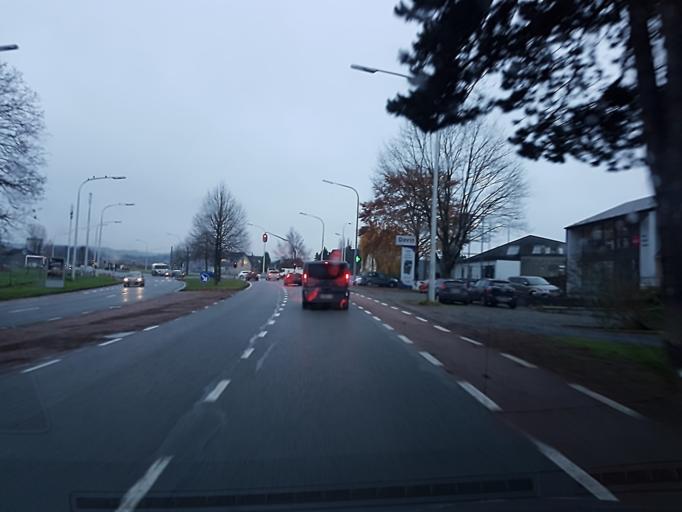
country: BE
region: Wallonia
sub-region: Province de Namur
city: Namur
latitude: 50.4505
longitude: 4.8937
